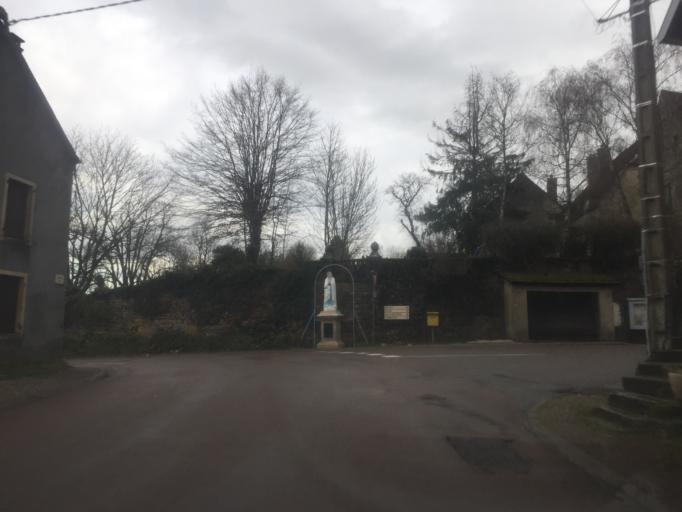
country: FR
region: Franche-Comte
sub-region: Departement de la Haute-Saone
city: Pesmes
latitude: 47.2227
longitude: 5.5346
